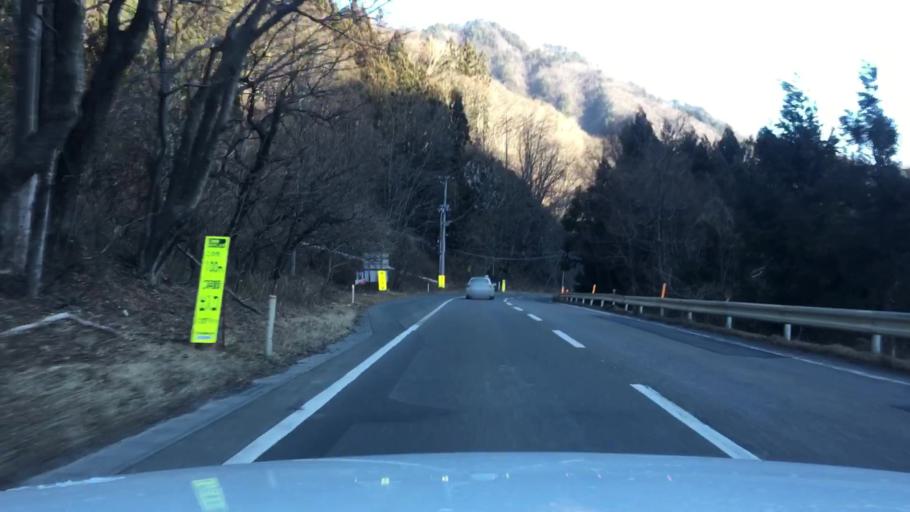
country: JP
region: Iwate
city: Miyako
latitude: 39.5966
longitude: 141.7216
